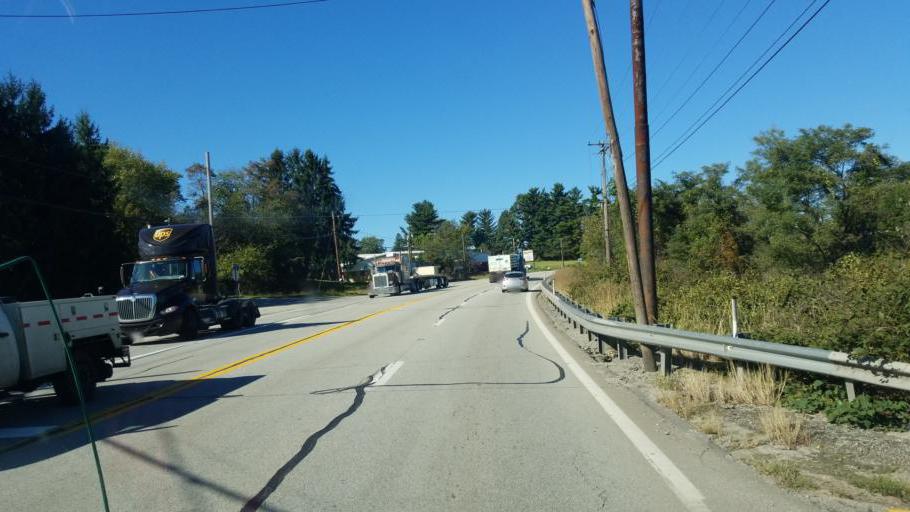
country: US
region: Pennsylvania
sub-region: Westmoreland County
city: Trafford
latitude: 40.3559
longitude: -79.7697
